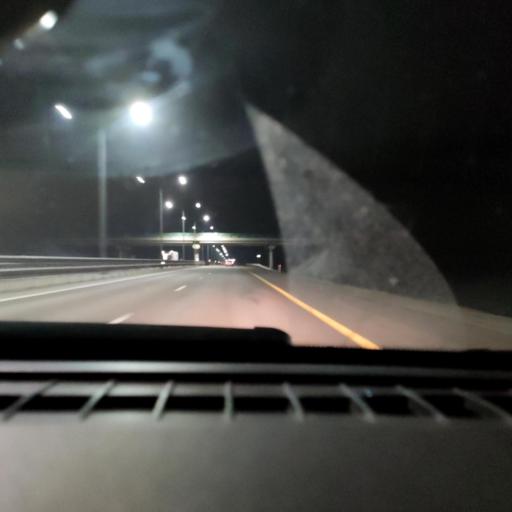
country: RU
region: Voronezj
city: Podkletnoye
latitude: 51.5708
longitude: 39.4723
